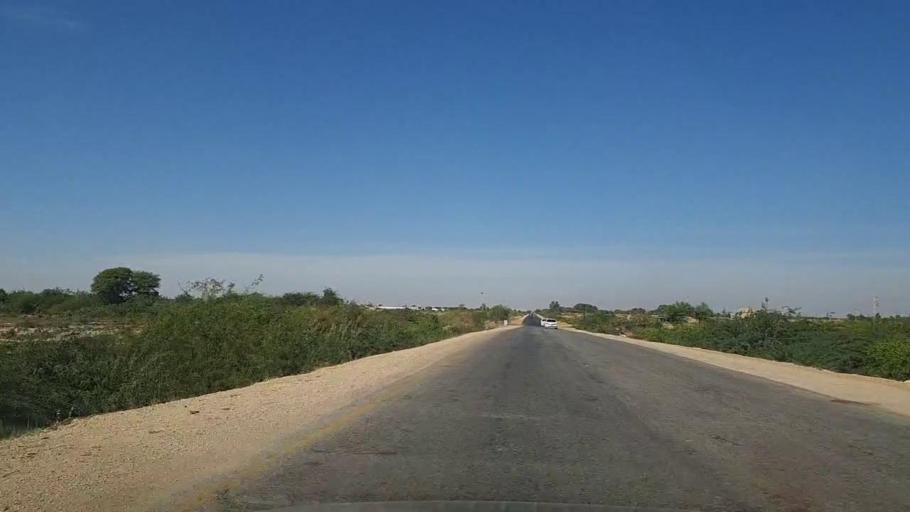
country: PK
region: Sindh
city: Kotri
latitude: 25.2230
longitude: 68.2375
